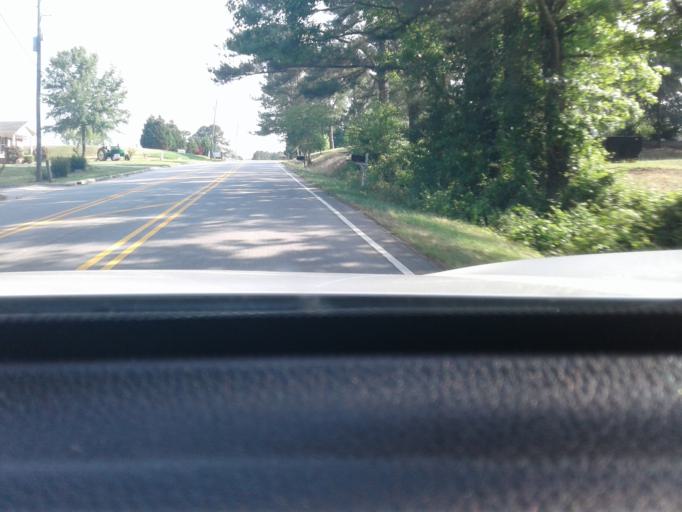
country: US
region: North Carolina
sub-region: Johnston County
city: Benson
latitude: 35.4018
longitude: -78.5416
